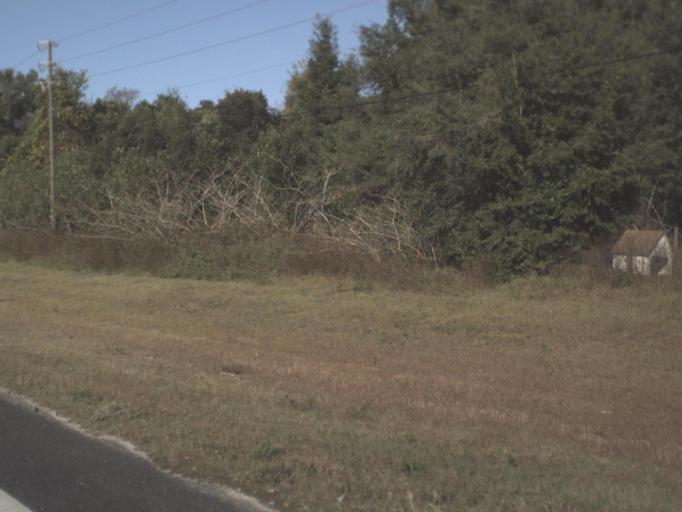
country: US
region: Florida
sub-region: Marion County
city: Belleview
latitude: 29.0261
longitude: -82.0872
